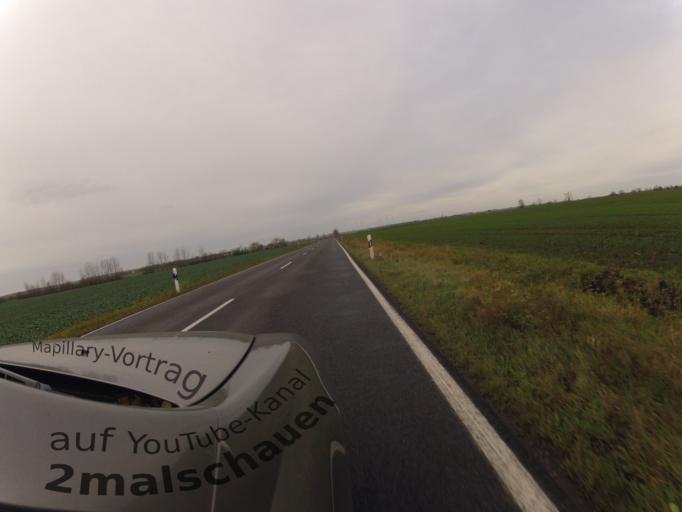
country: DE
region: Saxony-Anhalt
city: Peissen
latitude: 51.7243
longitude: 11.7297
